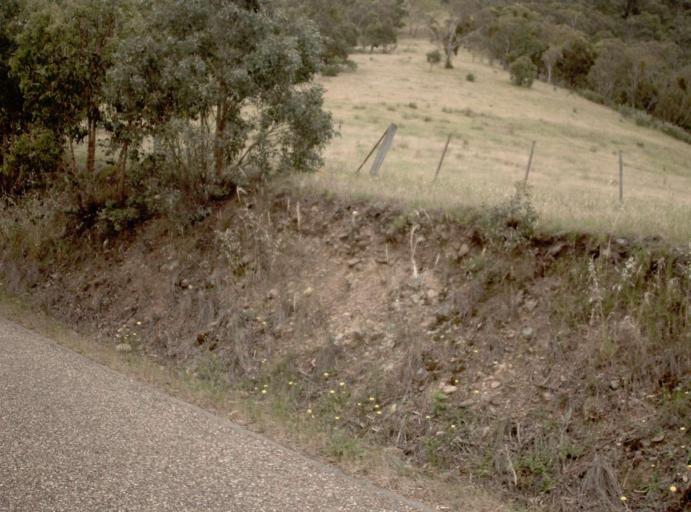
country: AU
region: Victoria
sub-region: East Gippsland
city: Bairnsdale
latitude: -37.5103
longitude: 147.2035
